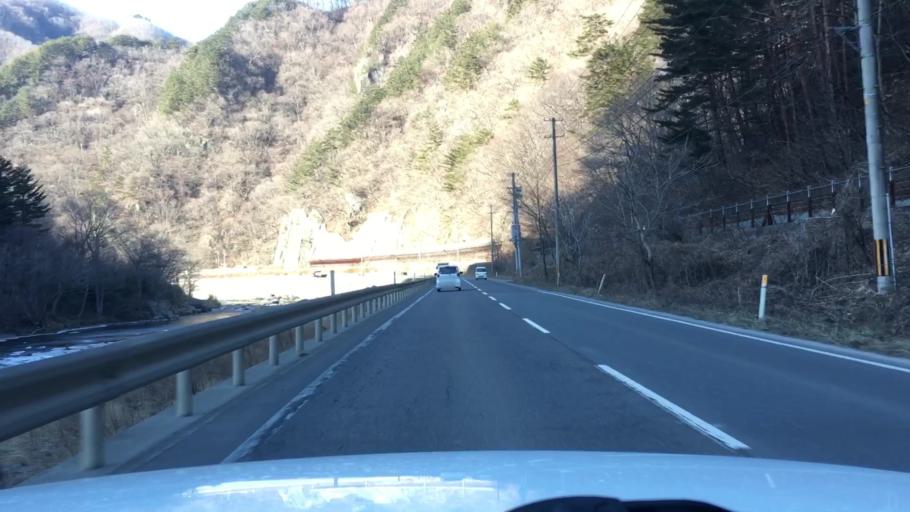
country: JP
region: Iwate
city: Miyako
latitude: 39.6089
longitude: 141.7793
